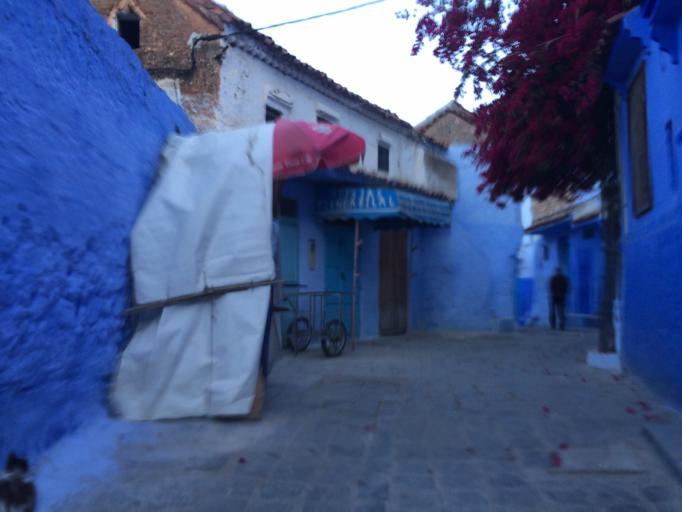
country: MA
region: Tanger-Tetouan
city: Chefchaouene
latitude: 35.1700
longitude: -5.2635
